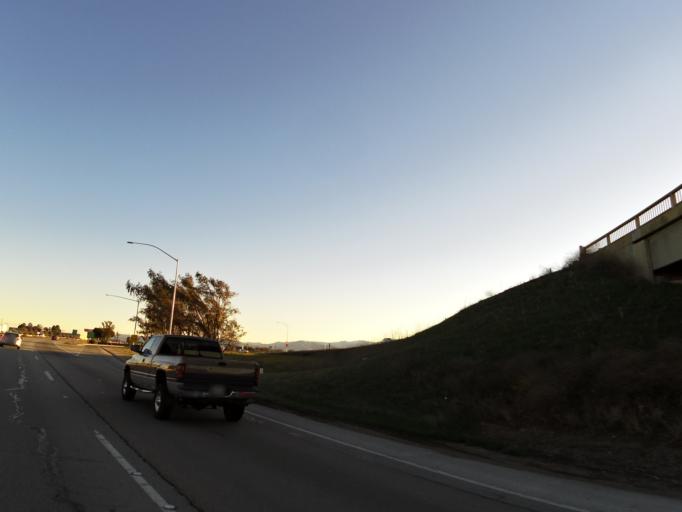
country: US
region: California
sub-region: Monterey County
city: Soledad
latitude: 36.4193
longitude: -121.3237
